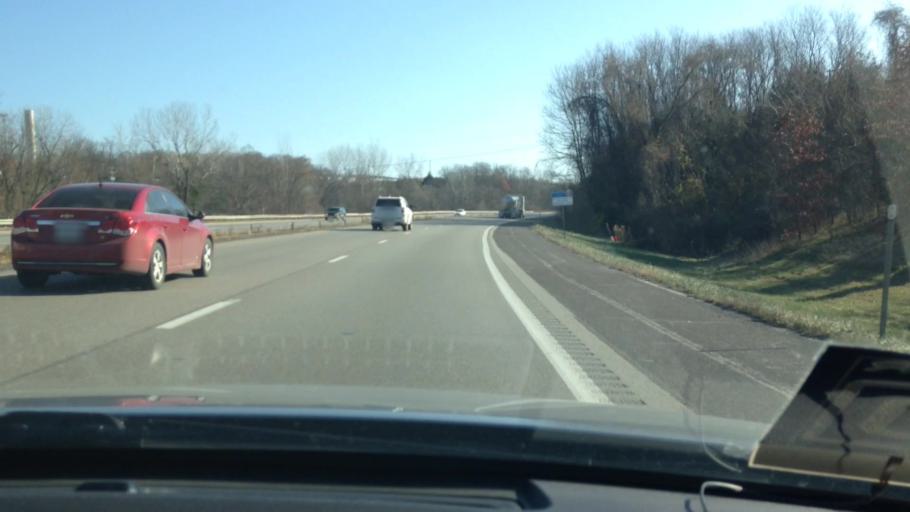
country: US
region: Missouri
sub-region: Platte County
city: Platte City
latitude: 39.3762
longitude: -94.7745
